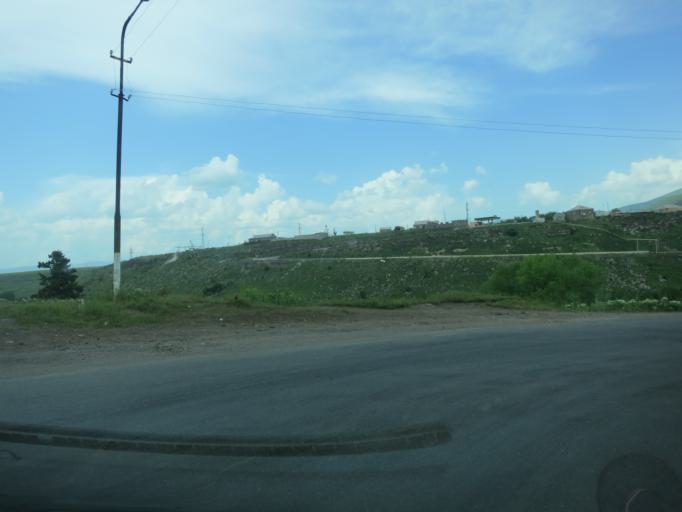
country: GE
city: Akhalk'alak'i
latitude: 41.4147
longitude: 43.4831
